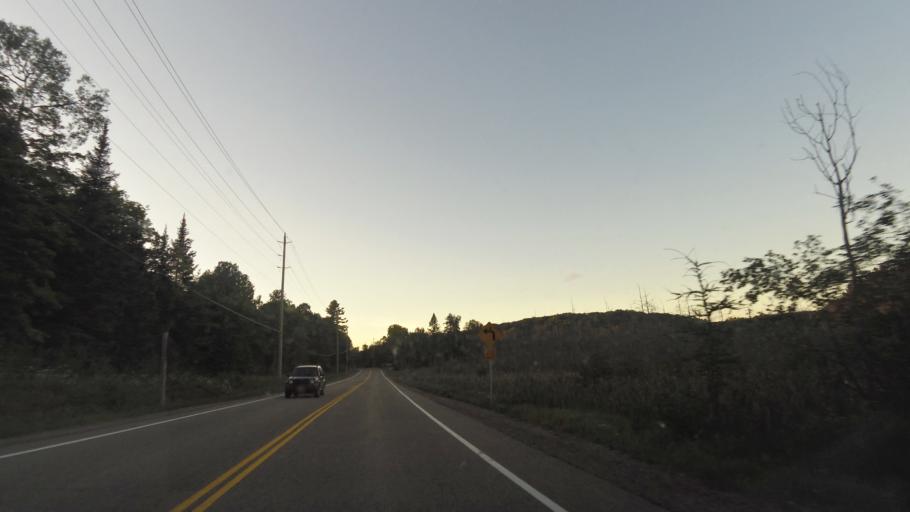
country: CA
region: Ontario
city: Bancroft
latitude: 45.0369
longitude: -78.4162
